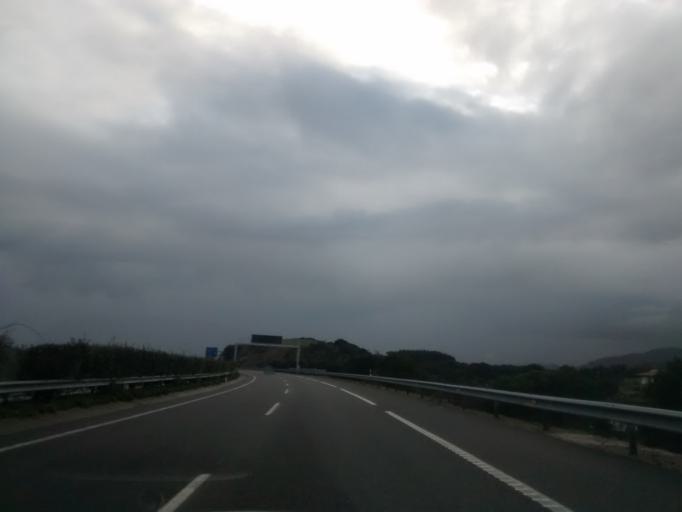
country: ES
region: Cantabria
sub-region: Provincia de Cantabria
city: Castro-Urdiales
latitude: 43.3979
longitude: -3.2486
